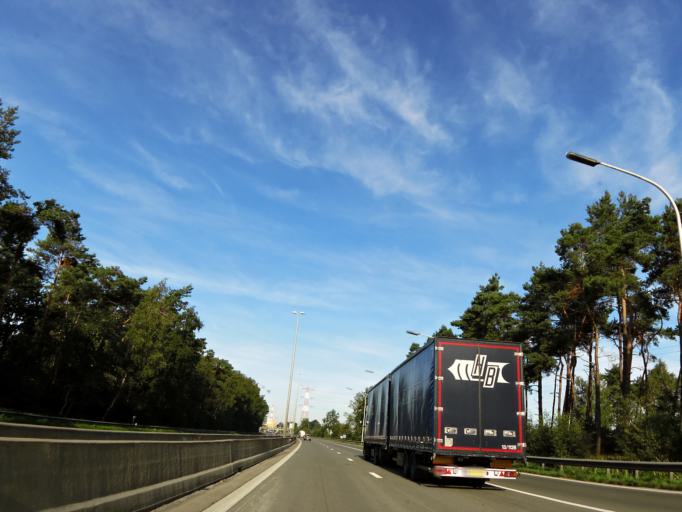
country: BE
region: Flanders
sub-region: Provincie Antwerpen
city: Grobbendonk
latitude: 51.1763
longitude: 4.7533
